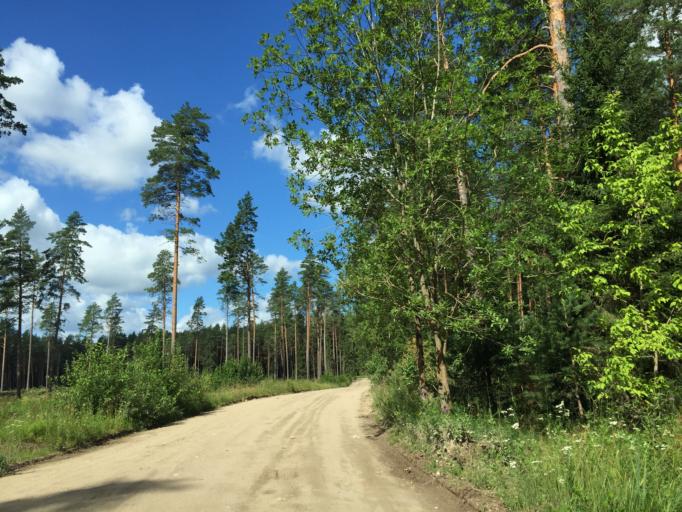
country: LV
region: Garkalne
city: Garkalne
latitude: 56.9715
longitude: 24.4671
